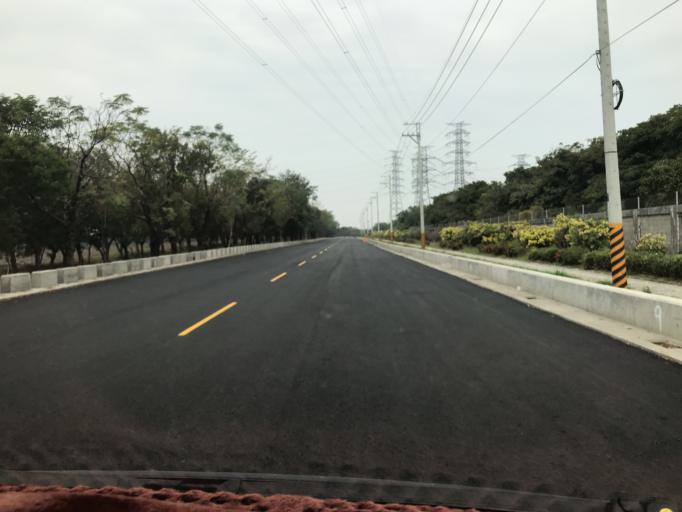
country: TW
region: Taiwan
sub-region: Pingtung
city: Pingtung
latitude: 22.4164
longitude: 120.6082
